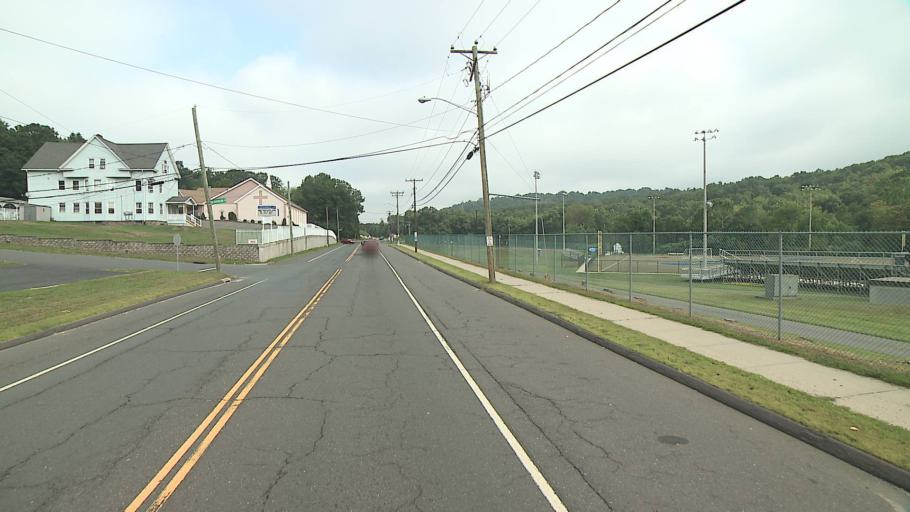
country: US
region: Connecticut
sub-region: Litchfield County
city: Oakville
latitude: 41.5785
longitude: -73.0710
